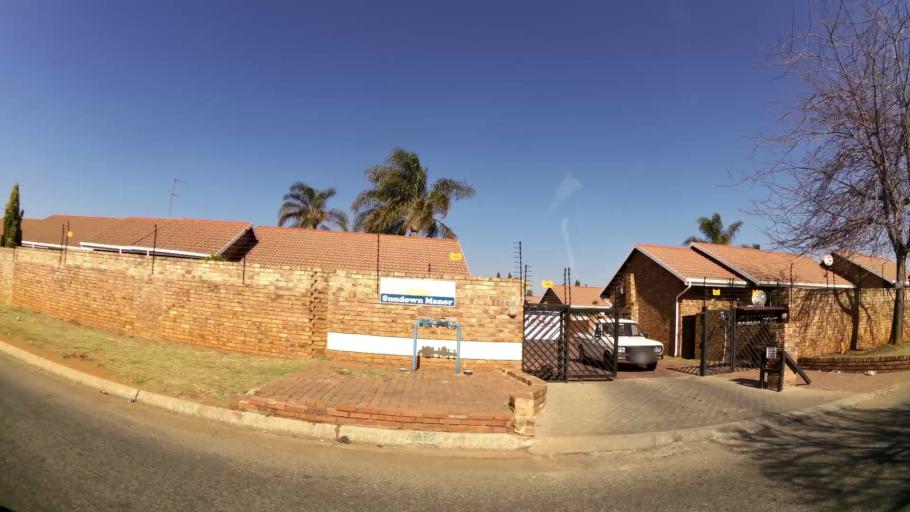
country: ZA
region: Gauteng
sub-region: Ekurhuleni Metropolitan Municipality
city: Tembisa
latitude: -26.0466
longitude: 28.2063
